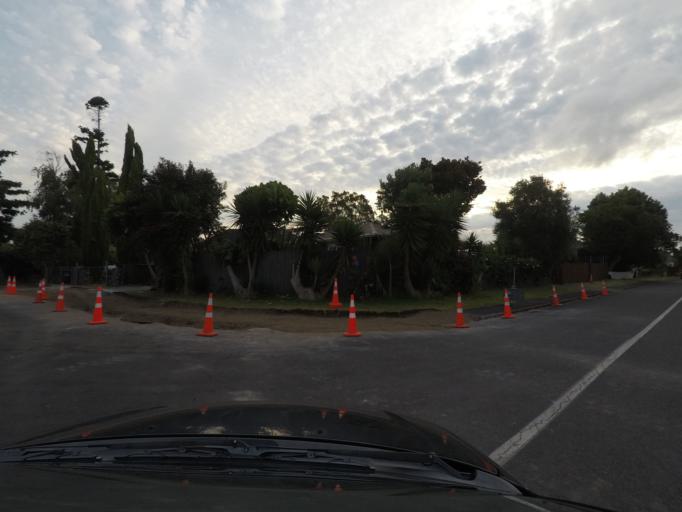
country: NZ
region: Auckland
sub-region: Auckland
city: Rosebank
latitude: -36.8359
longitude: 174.6533
